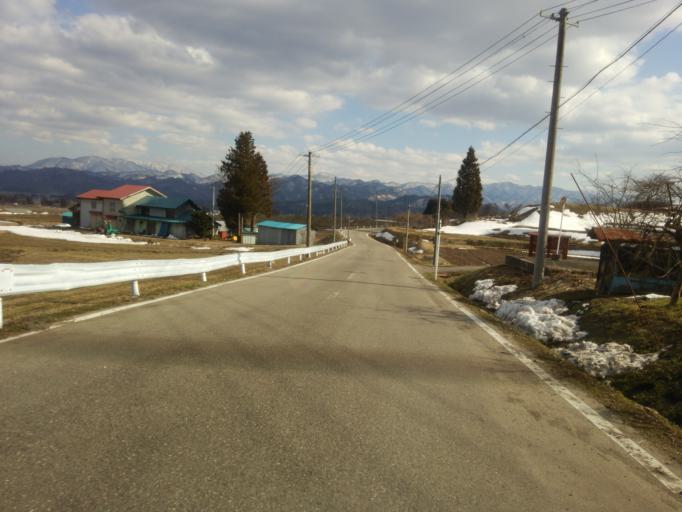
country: JP
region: Fukushima
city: Kitakata
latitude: 37.4537
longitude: 139.8029
